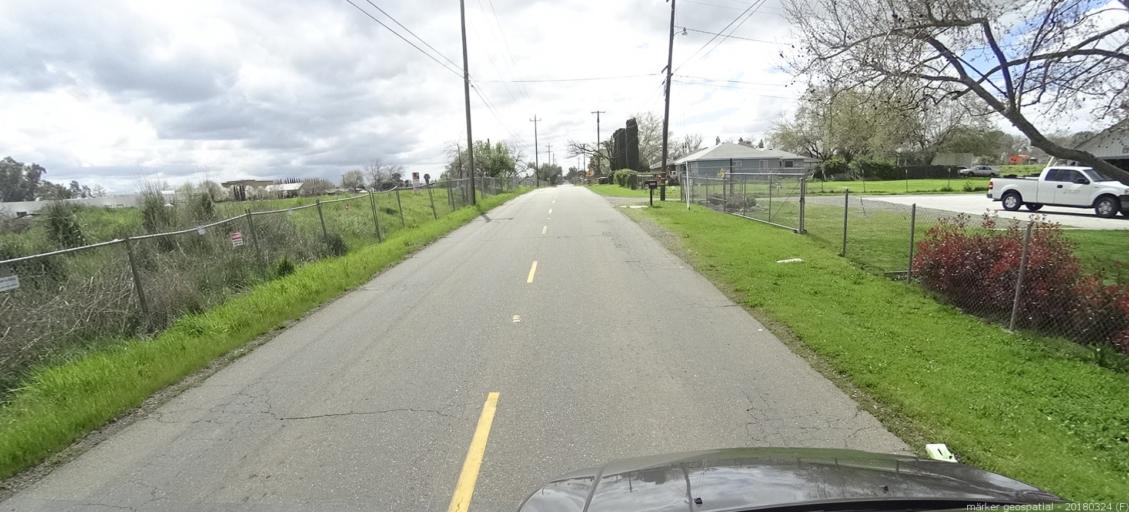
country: US
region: California
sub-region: Sacramento County
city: North Highlands
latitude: 38.6853
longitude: -121.3875
